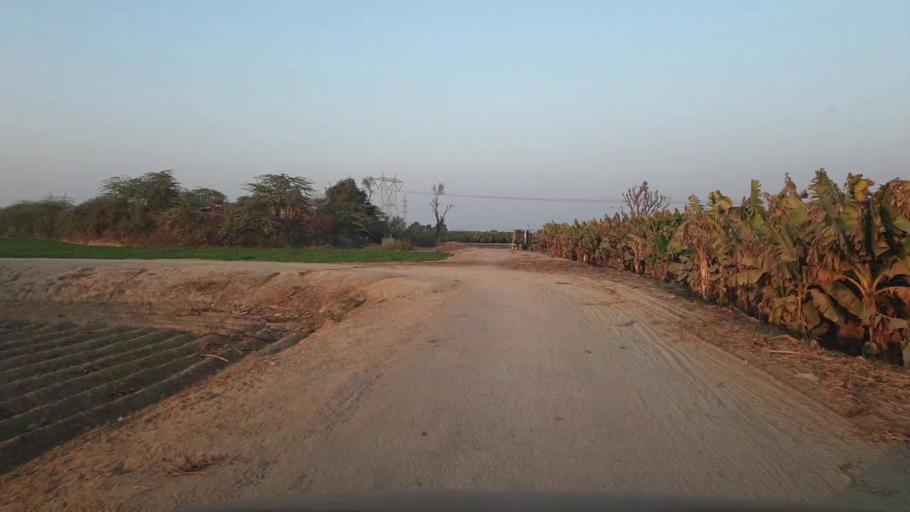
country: PK
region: Sindh
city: Bhit Shah
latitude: 25.8182
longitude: 68.5040
